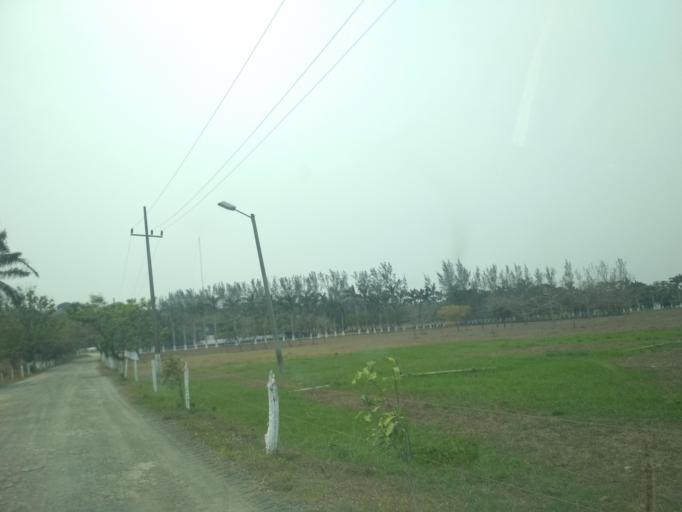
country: MX
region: Veracruz
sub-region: Veracruz
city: Lomas de Rio Medio Cuatro
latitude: 19.1708
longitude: -96.2118
